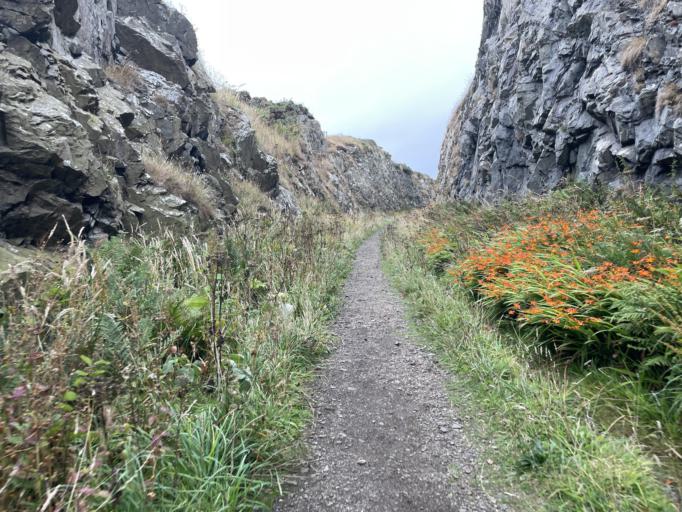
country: GB
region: Scotland
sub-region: Dumfries and Galloway
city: Stranraer
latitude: 54.8376
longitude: -5.1132
